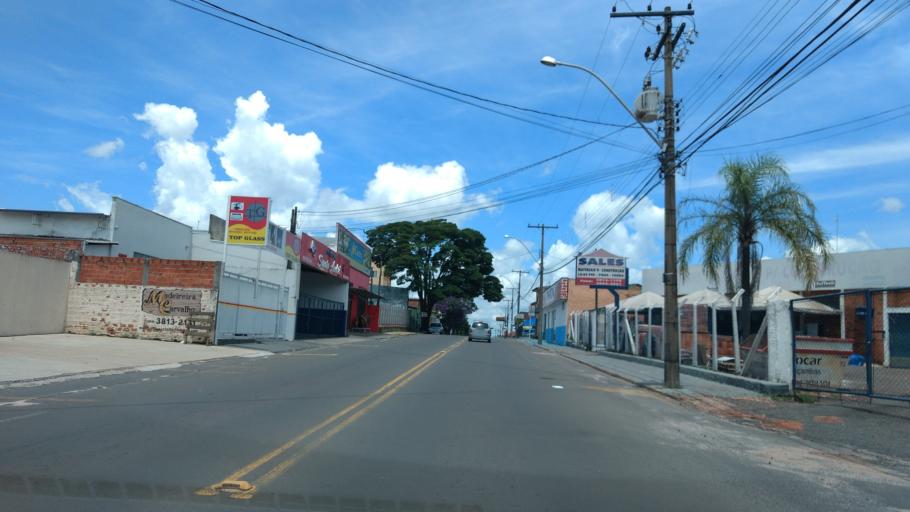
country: BR
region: Sao Paulo
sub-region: Botucatu
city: Botucatu
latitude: -22.8695
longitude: -48.4589
